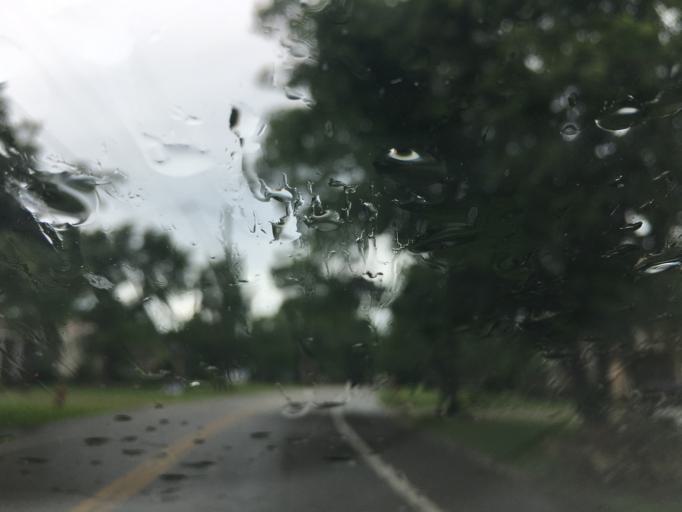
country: US
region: Tennessee
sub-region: Davidson County
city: Belle Meade
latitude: 36.0534
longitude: -86.9436
